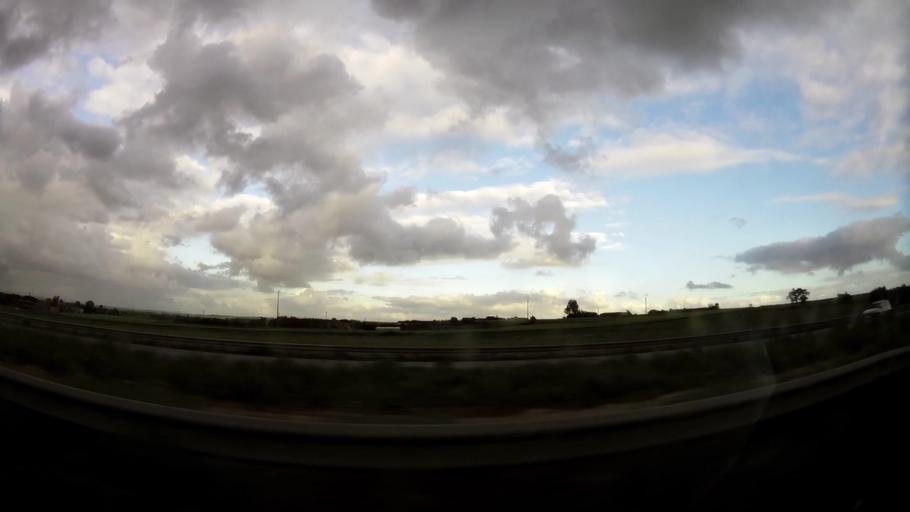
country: MA
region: Grand Casablanca
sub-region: Mediouna
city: Tit Mellil
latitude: 33.5811
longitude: -7.4527
